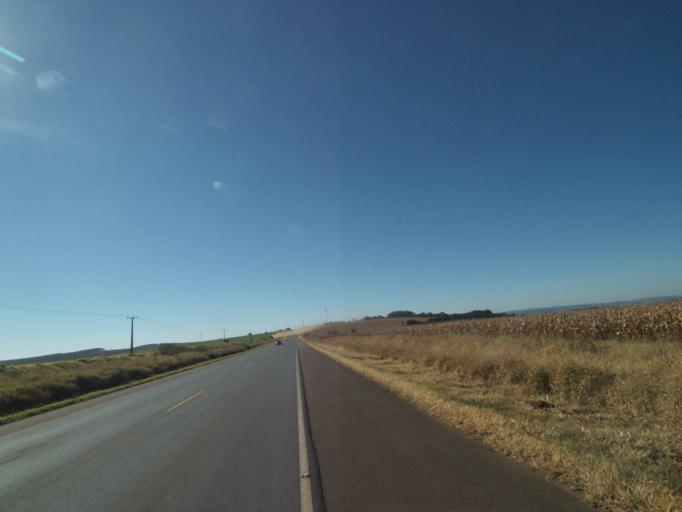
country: BR
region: Parana
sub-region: Tibagi
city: Tibagi
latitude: -24.3531
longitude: -50.3150
